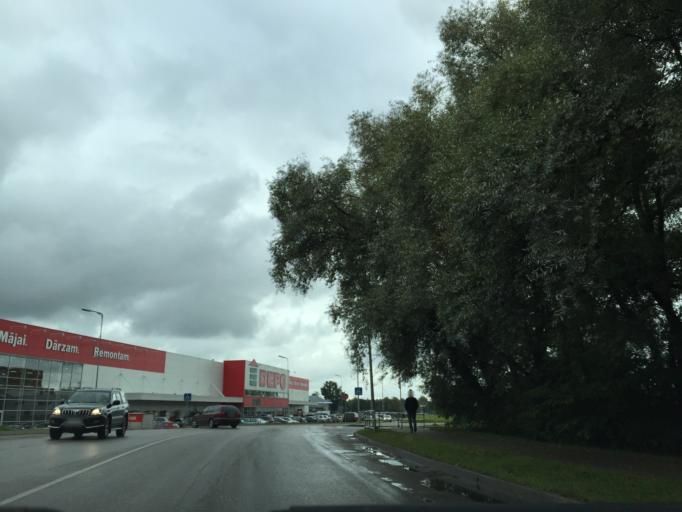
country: LV
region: Rezekne
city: Rezekne
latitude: 56.5182
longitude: 27.3483
